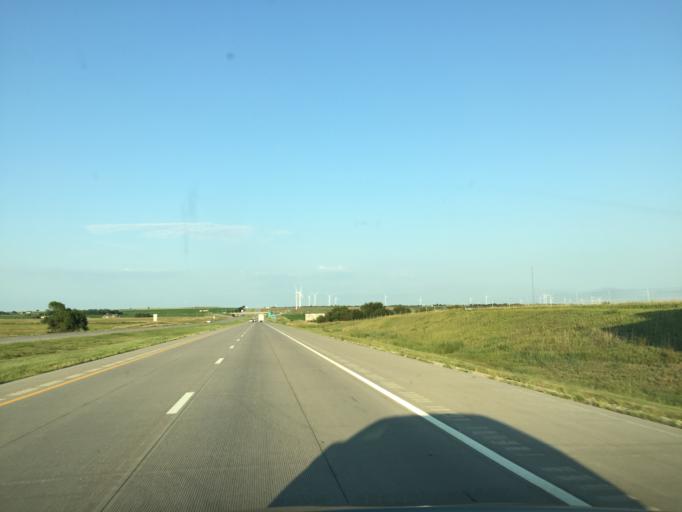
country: US
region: Kansas
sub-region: Ellsworth County
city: Ellsworth
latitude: 38.8486
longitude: -98.4812
